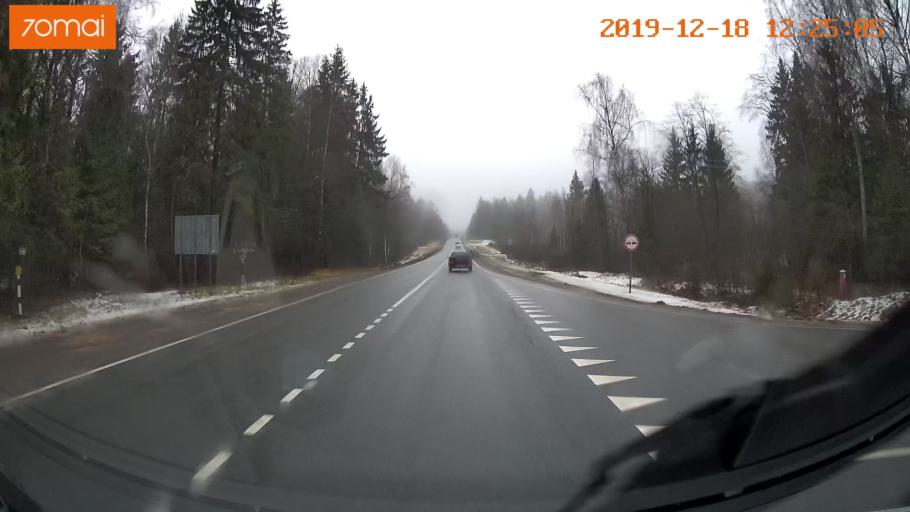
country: RU
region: Moskovskaya
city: Novopetrovskoye
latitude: 56.0332
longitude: 36.5001
